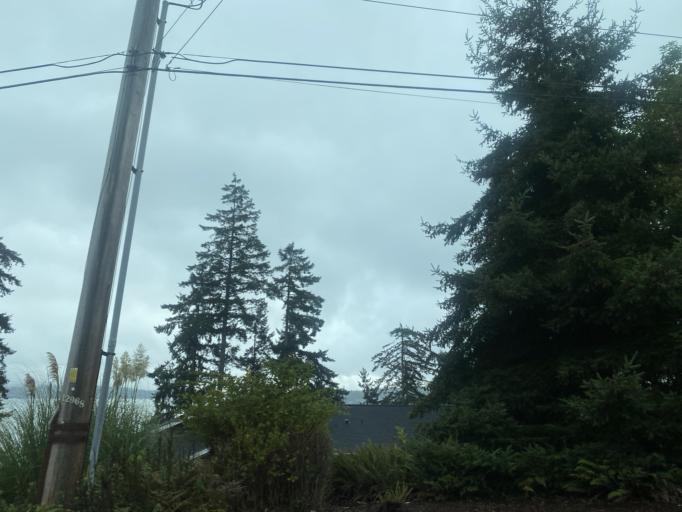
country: US
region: Washington
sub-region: Island County
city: Freeland
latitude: 48.0866
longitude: -122.5622
